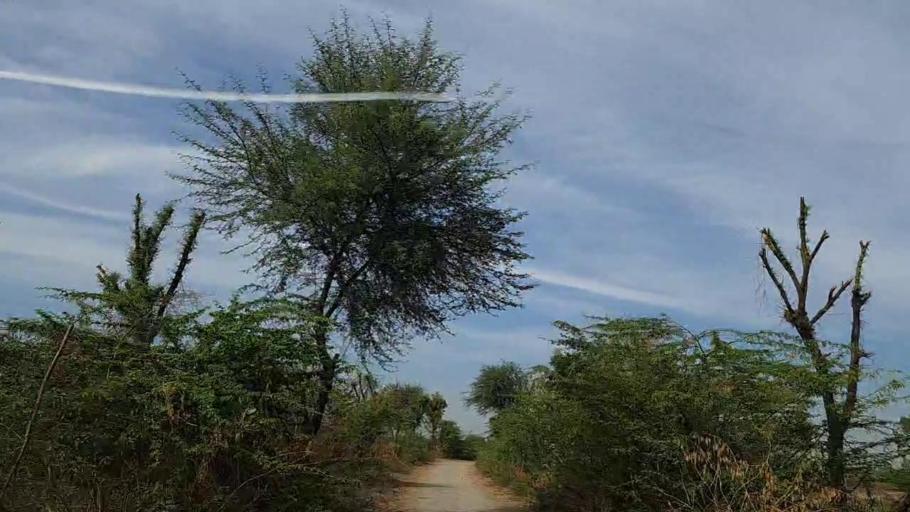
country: PK
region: Sindh
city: Dhoro Naro
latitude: 25.5087
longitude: 69.5259
